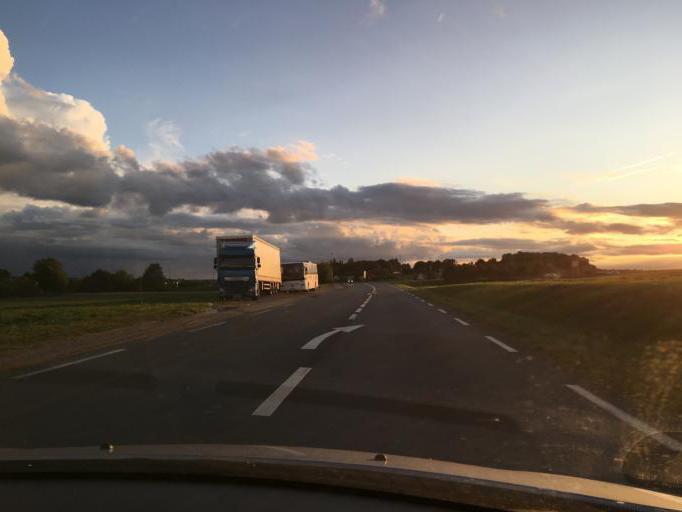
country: FR
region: Centre
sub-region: Departement d'Eure-et-Loir
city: Chateaudun
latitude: 48.0840
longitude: 1.3166
